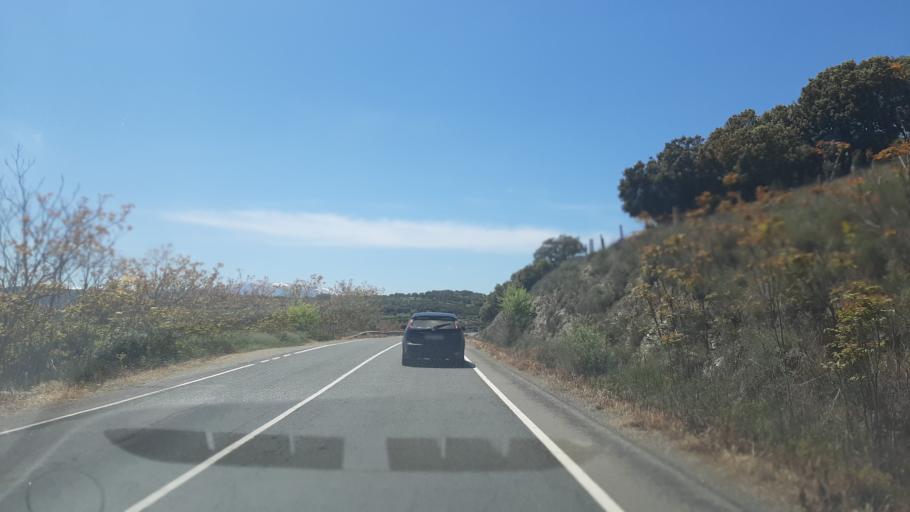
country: ES
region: Castille and Leon
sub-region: Provincia de Salamanca
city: Guijo de Avila
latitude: 40.5532
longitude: -5.6334
